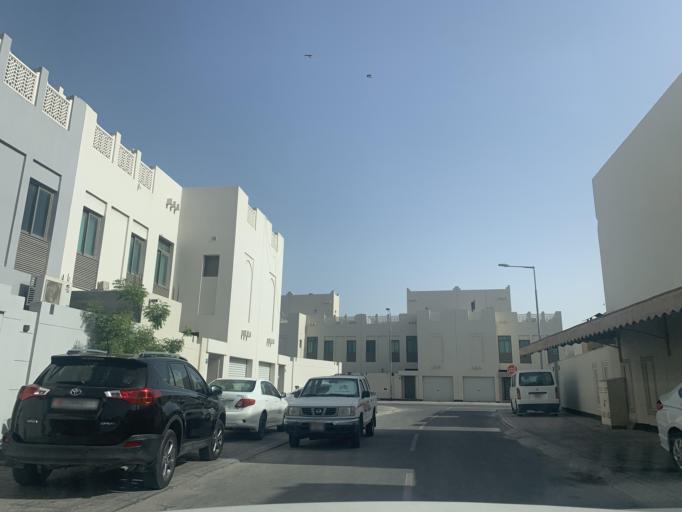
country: BH
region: Northern
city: Sitrah
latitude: 26.1598
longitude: 50.6288
